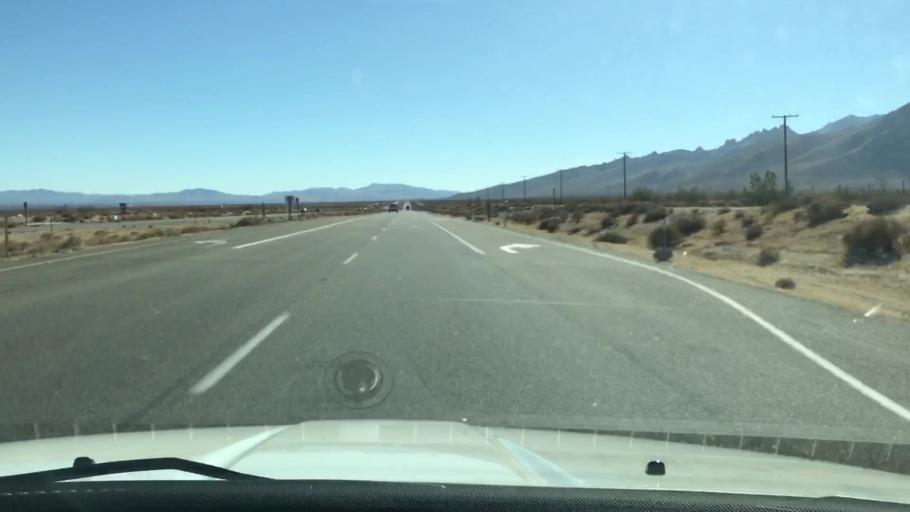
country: US
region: California
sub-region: Kern County
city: Inyokern
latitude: 35.7698
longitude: -117.8719
